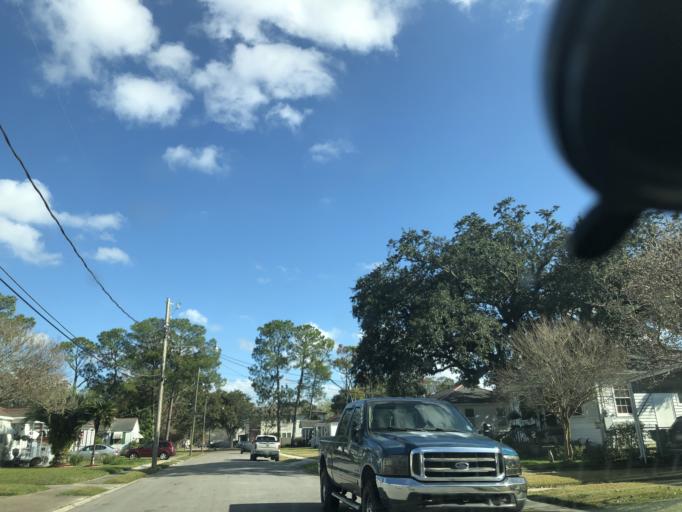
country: US
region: Louisiana
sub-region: Jefferson Parish
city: Metairie Terrace
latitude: 29.9798
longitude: -90.1628
